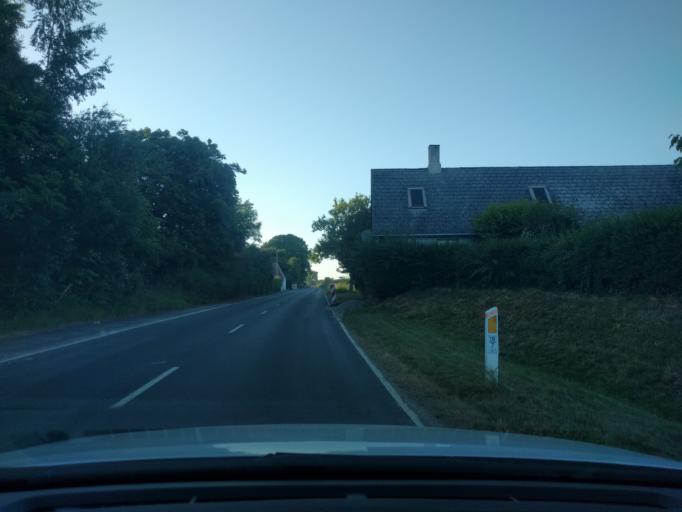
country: DK
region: South Denmark
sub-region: Kerteminde Kommune
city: Kerteminde
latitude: 55.5983
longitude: 10.6256
